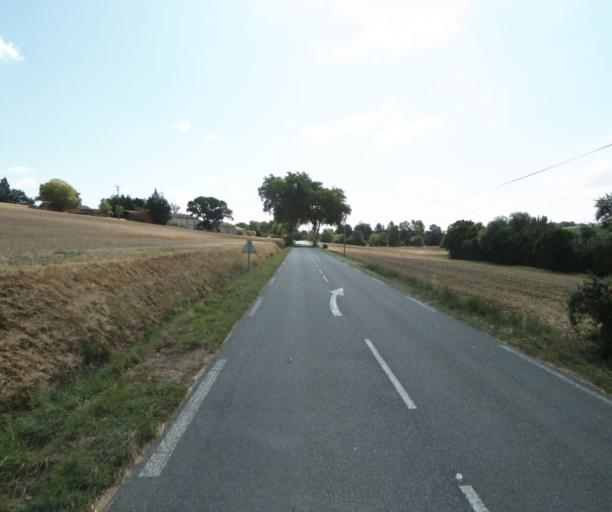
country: FR
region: Midi-Pyrenees
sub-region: Departement de la Haute-Garonne
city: Avignonet-Lauragais
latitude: 43.4469
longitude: 1.7944
